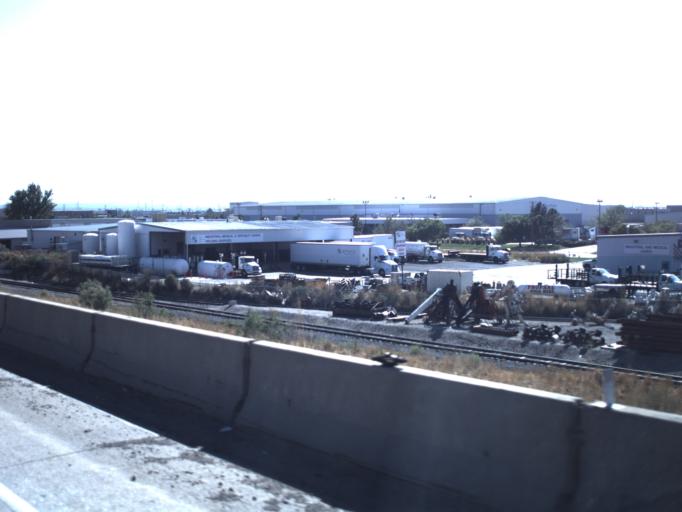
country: US
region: Utah
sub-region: Salt Lake County
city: Salt Lake City
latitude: 40.7447
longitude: -111.9493
